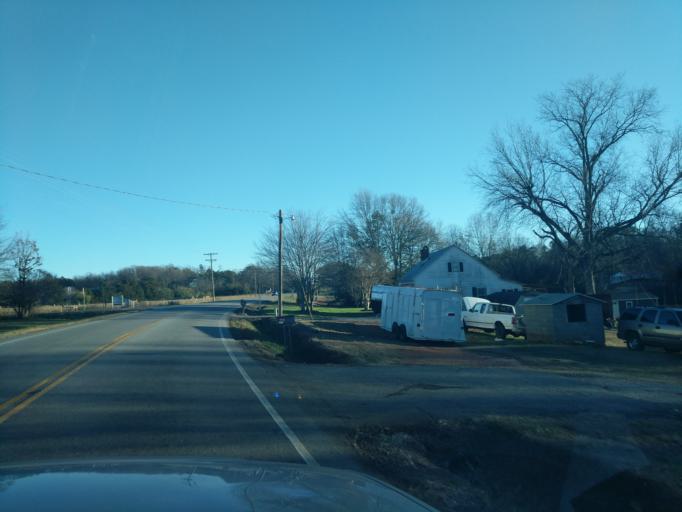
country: US
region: South Carolina
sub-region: Oconee County
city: Westminster
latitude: 34.6193
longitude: -83.0462
